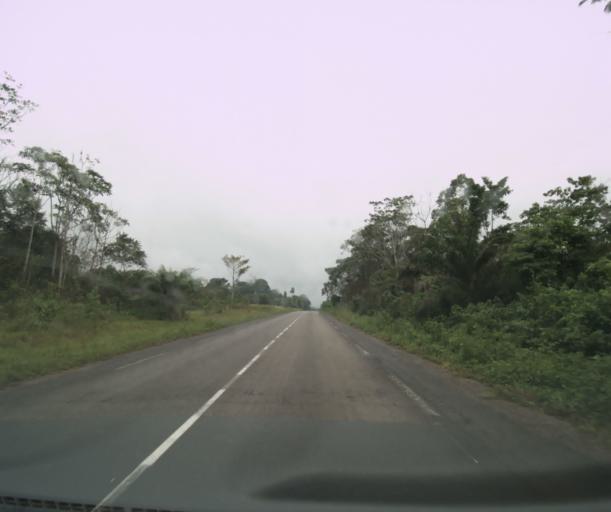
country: CM
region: Littoral
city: Dizangue
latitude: 3.3581
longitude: 10.1019
